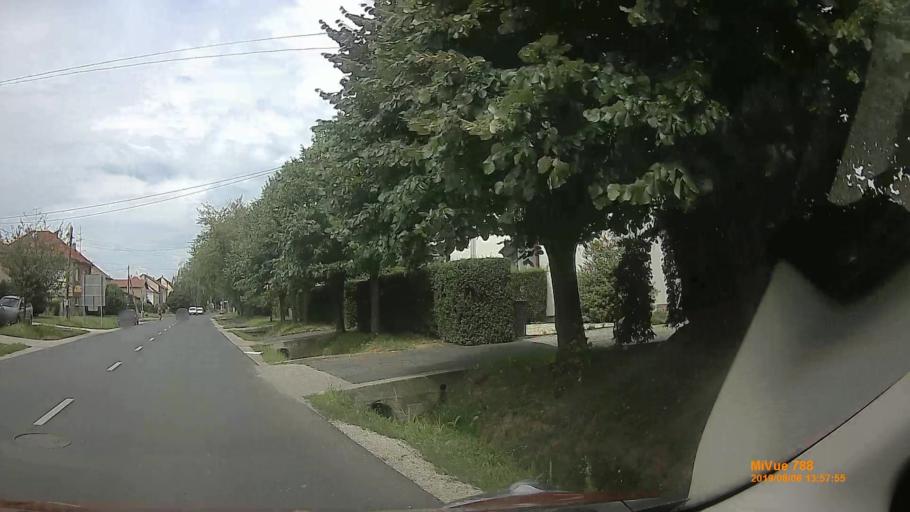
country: HU
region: Vas
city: Szombathely
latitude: 47.2512
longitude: 16.6064
